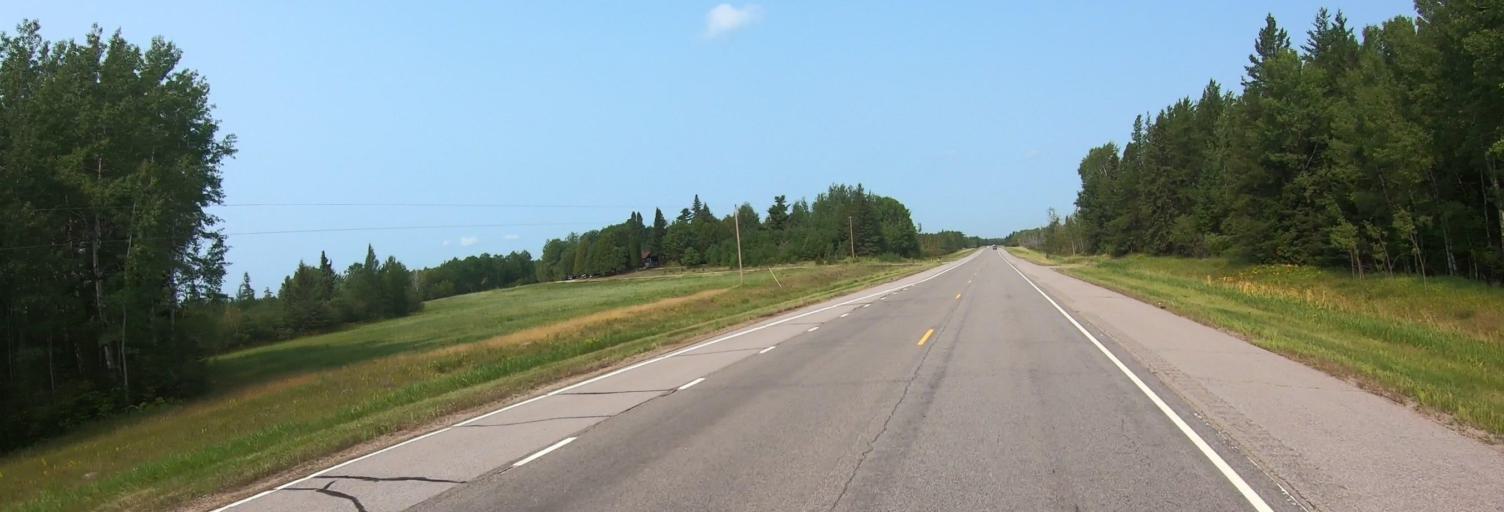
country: US
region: Minnesota
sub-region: Saint Louis County
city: Mountain Iron
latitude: 47.8681
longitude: -92.7408
